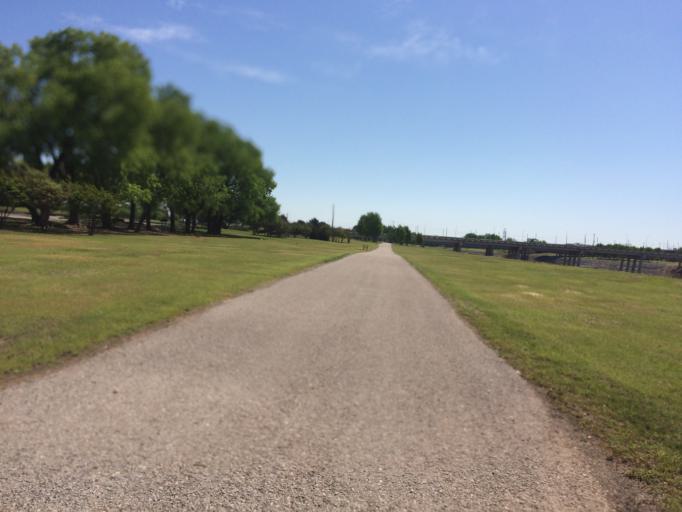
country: US
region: Oklahoma
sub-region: Oklahoma County
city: Oklahoma City
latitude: 35.4491
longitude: -97.5198
